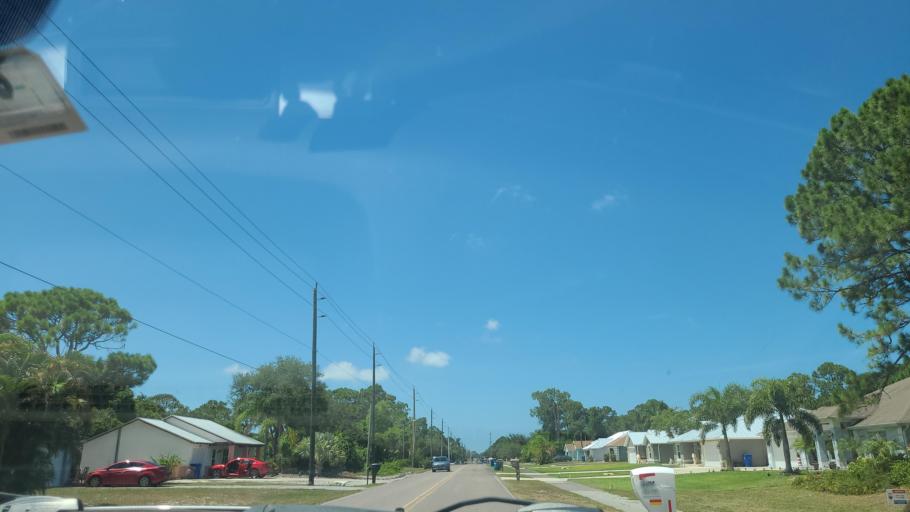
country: US
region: Florida
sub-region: Indian River County
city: Sebastian
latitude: 27.7665
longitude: -80.4659
